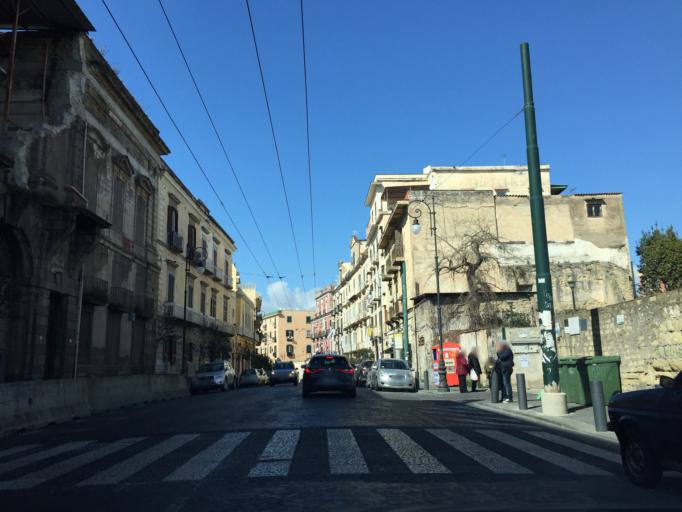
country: IT
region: Campania
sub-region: Provincia di Napoli
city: Portici
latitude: 40.8201
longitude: 14.3278
